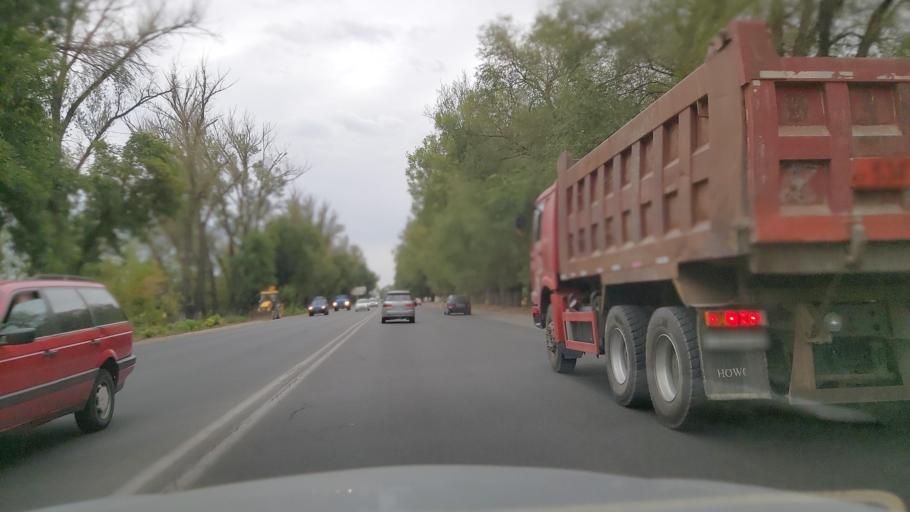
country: KZ
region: Almaty Oblysy
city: Energeticheskiy
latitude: 43.3314
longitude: 77.0355
